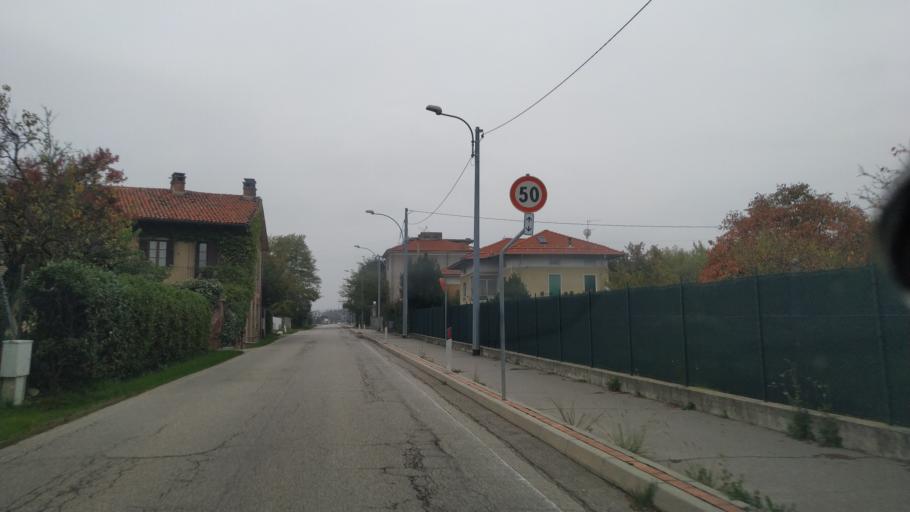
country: IT
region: Piedmont
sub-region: Provincia di Biella
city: Lessona
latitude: 45.5702
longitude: 8.2096
